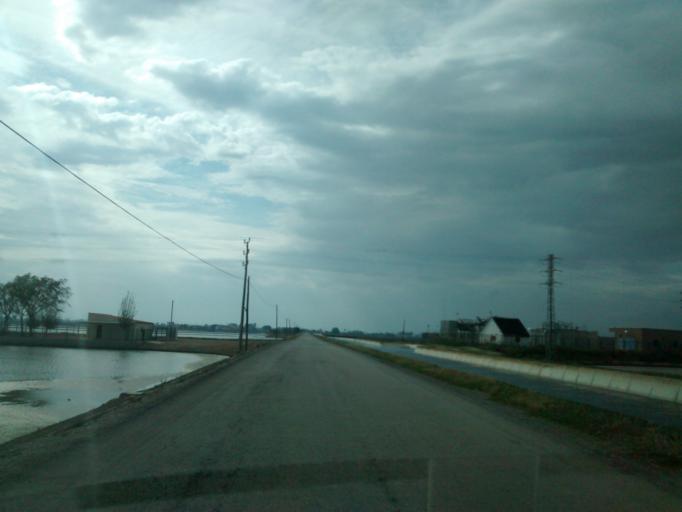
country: ES
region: Catalonia
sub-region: Provincia de Tarragona
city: Deltebre
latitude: 40.6979
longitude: 0.7552
